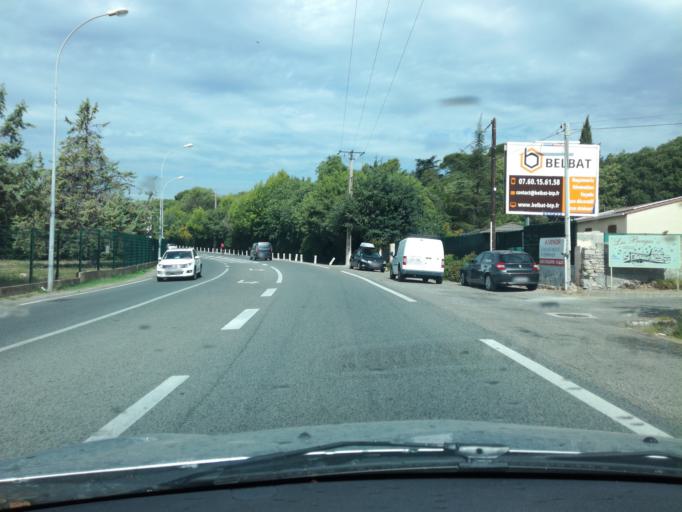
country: FR
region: Provence-Alpes-Cote d'Azur
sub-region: Departement du Var
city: Draguignan
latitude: 43.5265
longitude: 6.4590
